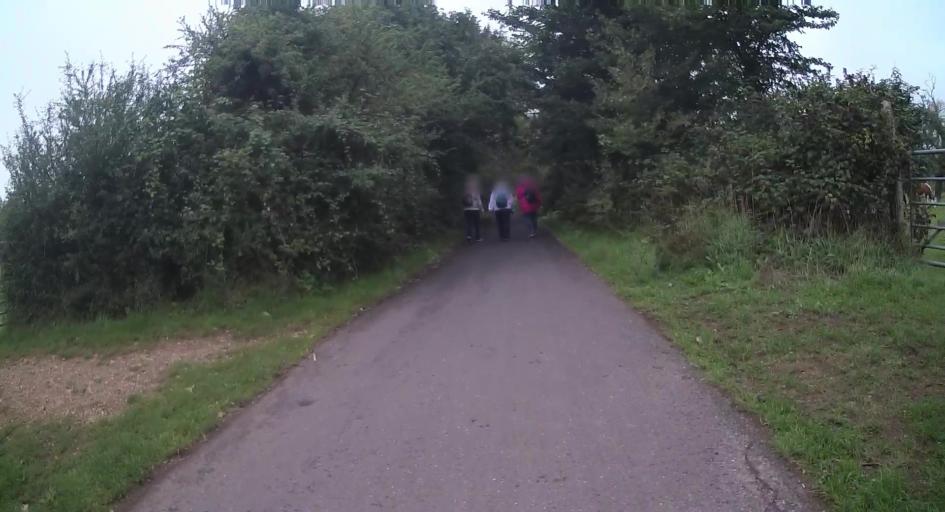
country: GB
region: England
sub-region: Isle of Wight
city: Sandown
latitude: 50.6650
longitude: -1.1782
